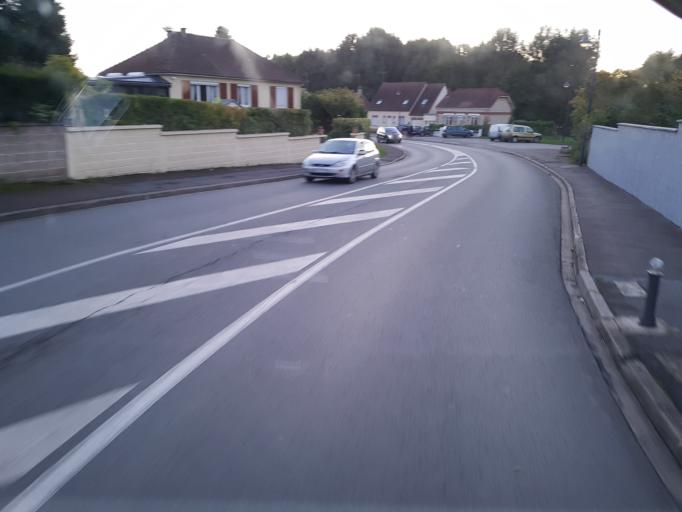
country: FR
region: Picardie
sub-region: Departement de la Somme
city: Ailly-sur-Noye
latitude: 49.7531
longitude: 2.3600
